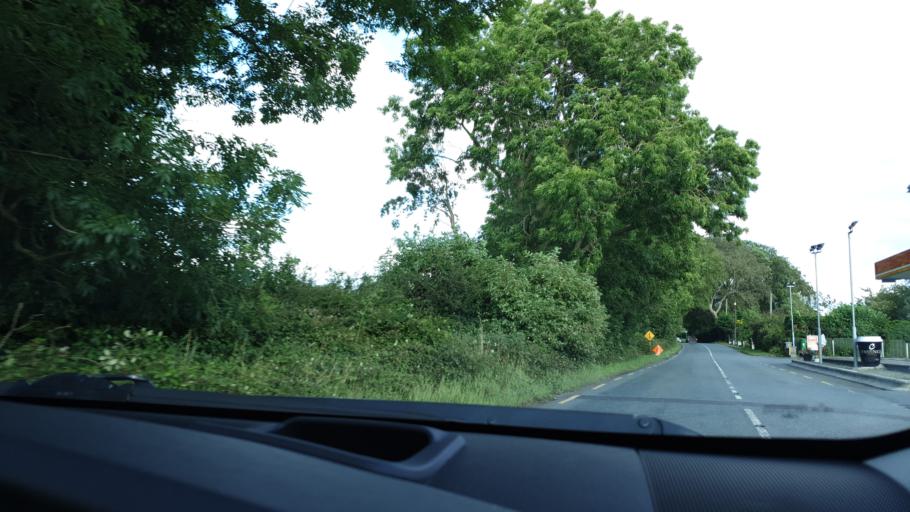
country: IE
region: Leinster
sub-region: An Mhi
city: Ashbourne
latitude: 53.4958
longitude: -6.3963
